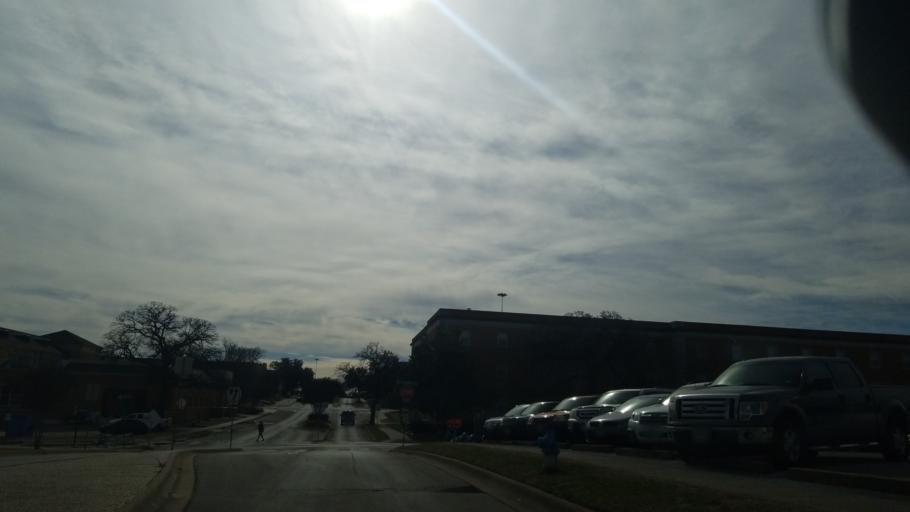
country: US
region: Texas
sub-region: Denton County
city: Denton
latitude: 33.2133
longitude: -97.1507
